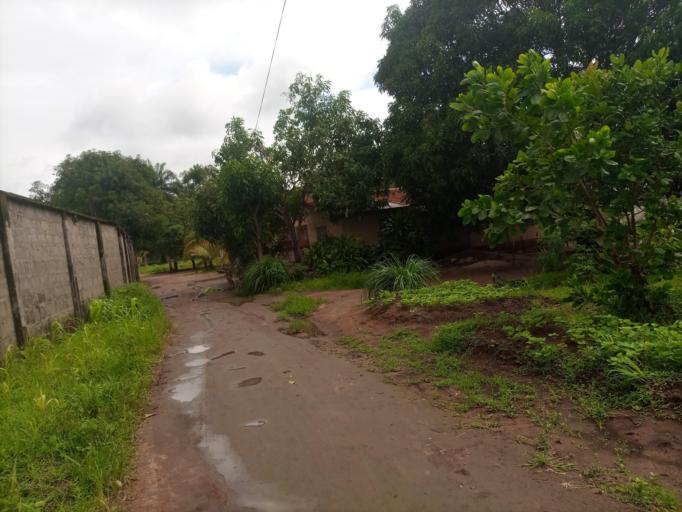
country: SL
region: Northern Province
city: Sawkta
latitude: 8.6250
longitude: -13.2021
